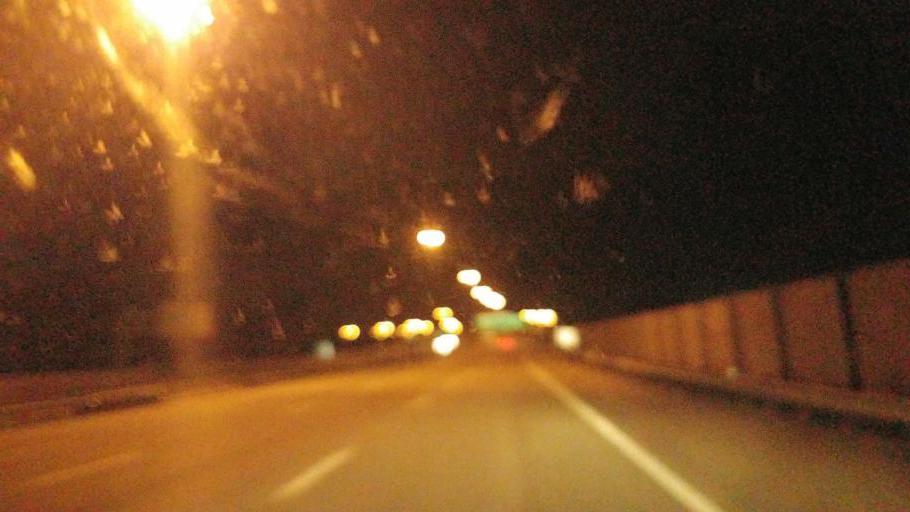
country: US
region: Ohio
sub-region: Cuyahoga County
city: North Randall
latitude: 41.4262
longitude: -81.5164
